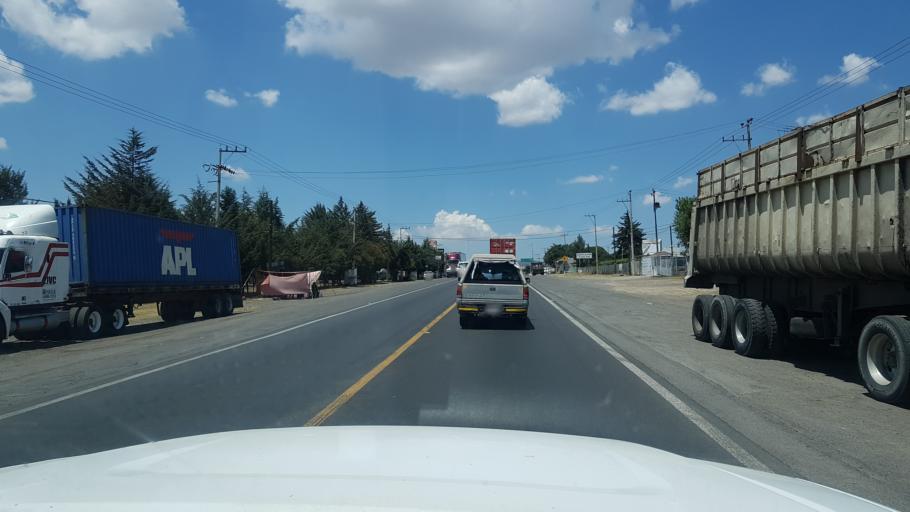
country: MX
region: Hidalgo
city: Calpulalpan
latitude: 19.5893
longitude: -98.5539
